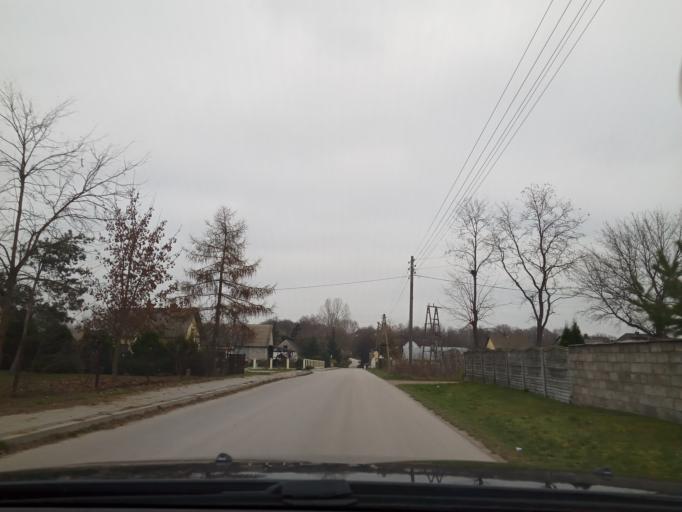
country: PL
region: Swietokrzyskie
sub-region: Powiat jedrzejowski
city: Imielno
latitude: 50.6014
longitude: 20.4862
